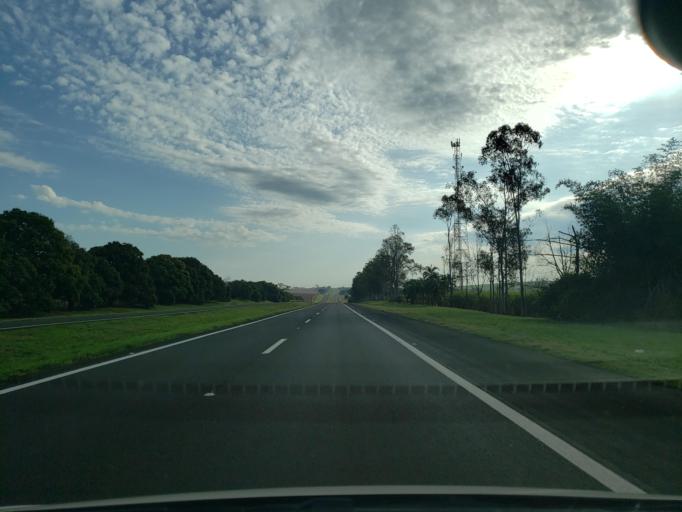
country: BR
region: Sao Paulo
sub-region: Valparaiso
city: Valparaiso
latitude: -21.2067
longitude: -50.7632
